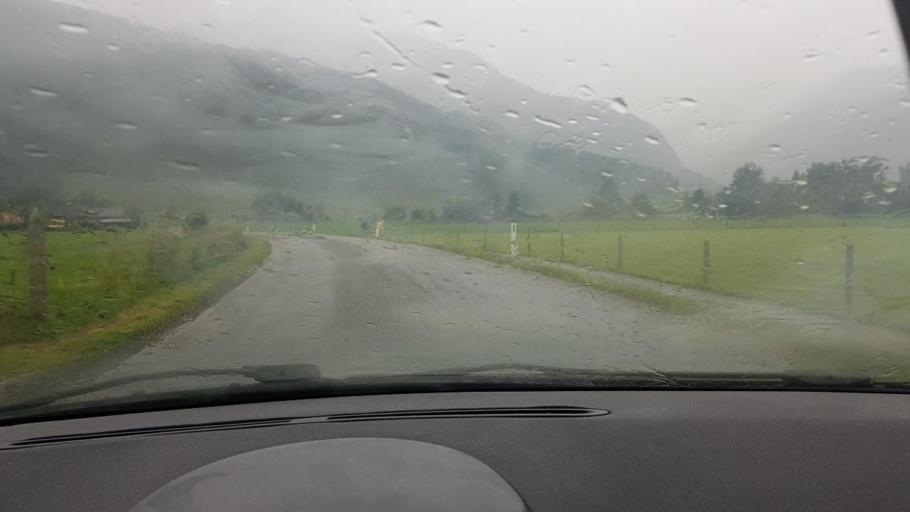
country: AT
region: Salzburg
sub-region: Politischer Bezirk Zell am See
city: Kaprun
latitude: 47.2852
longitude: 12.7843
